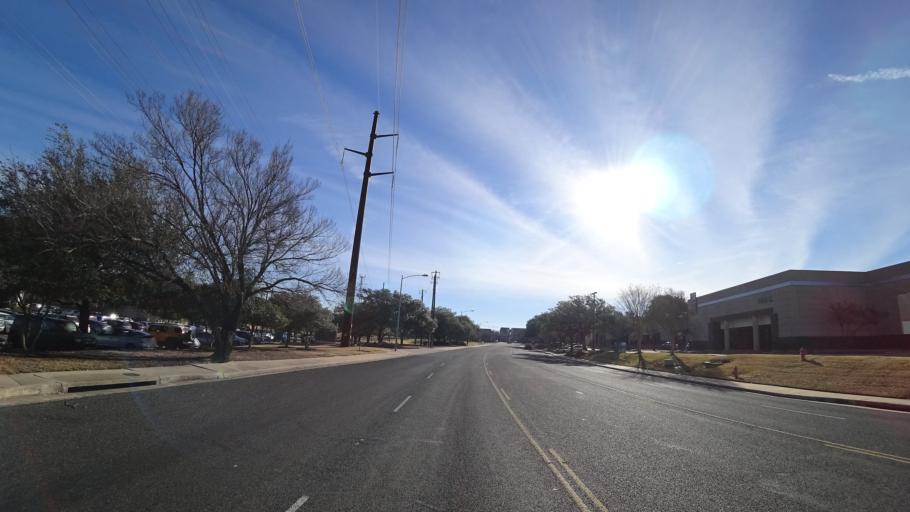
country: US
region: Texas
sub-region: Travis County
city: Wells Branch
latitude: 30.3956
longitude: -97.7087
